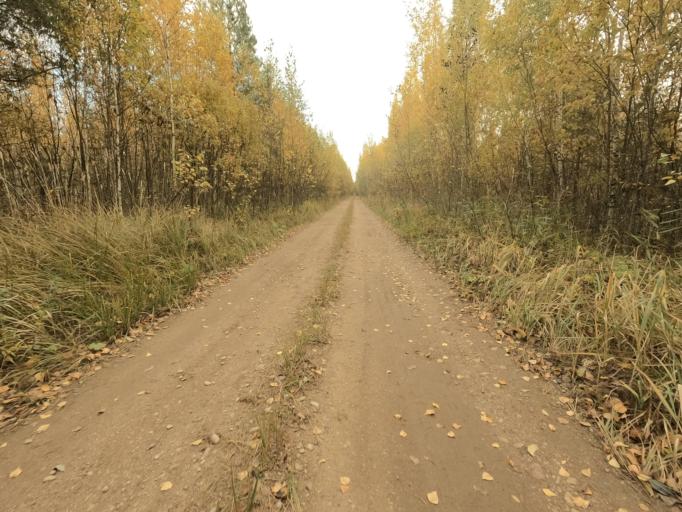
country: RU
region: Novgorod
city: Pankovka
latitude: 58.8762
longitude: 30.8712
